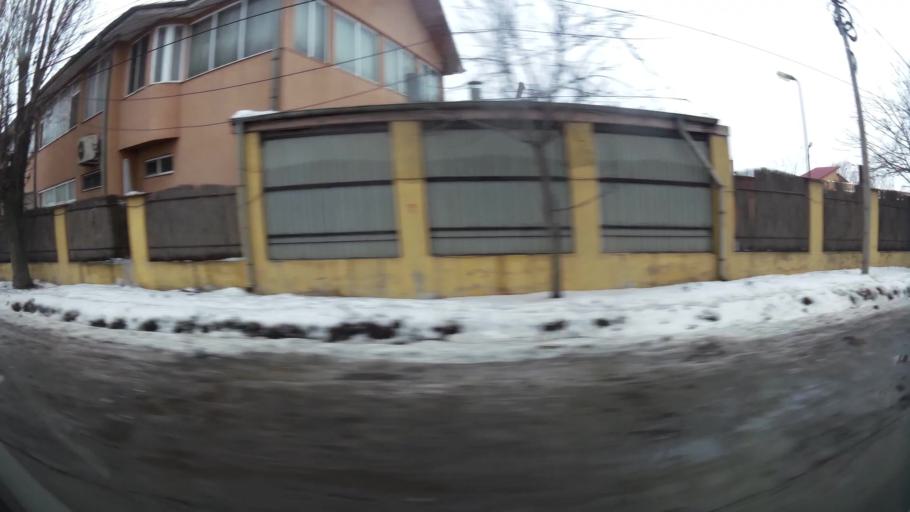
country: RO
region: Ilfov
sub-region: Comuna Bragadiru
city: Bragadiru
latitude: 44.3836
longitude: 25.9926
